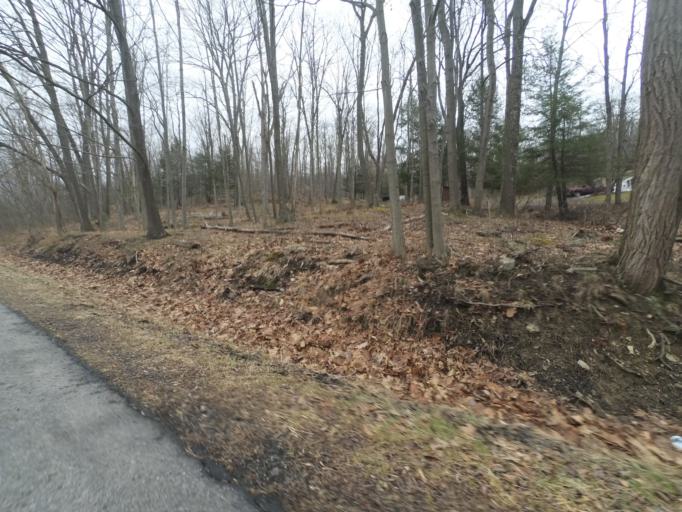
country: US
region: Pennsylvania
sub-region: Centre County
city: Stormstown
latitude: 40.8603
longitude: -78.0112
